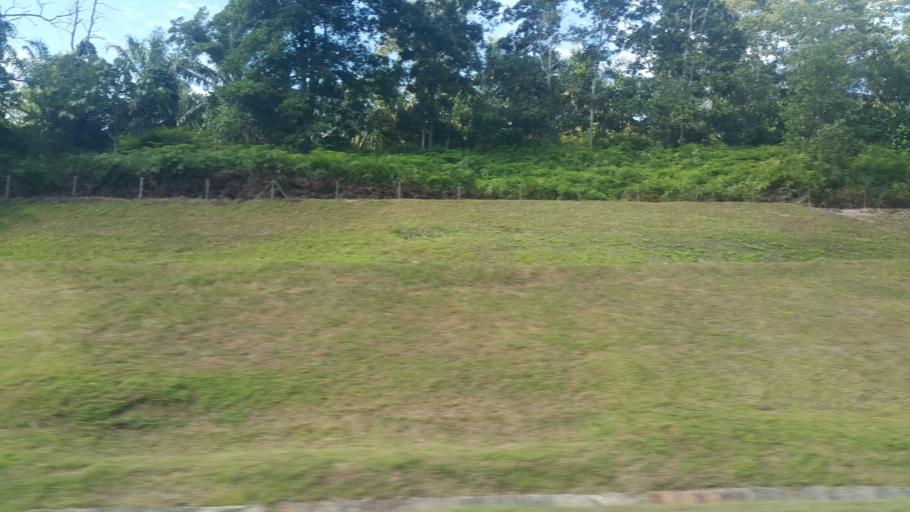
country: MY
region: Johor
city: Kelapa Sawit
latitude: 1.7229
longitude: 103.4312
